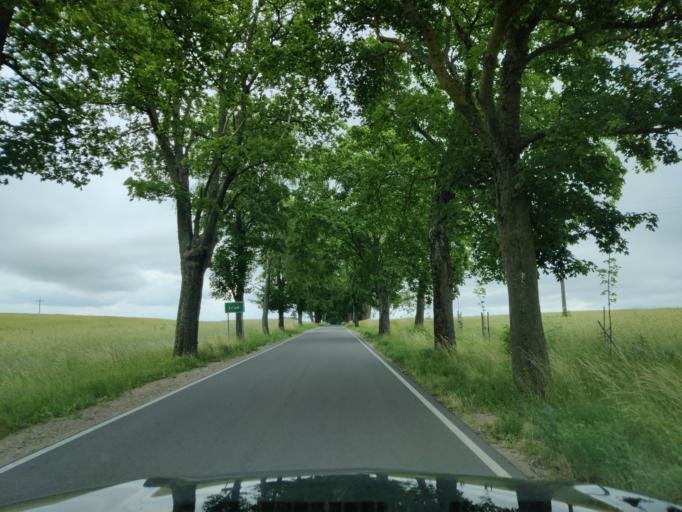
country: PL
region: Warmian-Masurian Voivodeship
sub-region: Powiat mragowski
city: Mikolajki
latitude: 53.8617
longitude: 21.6038
